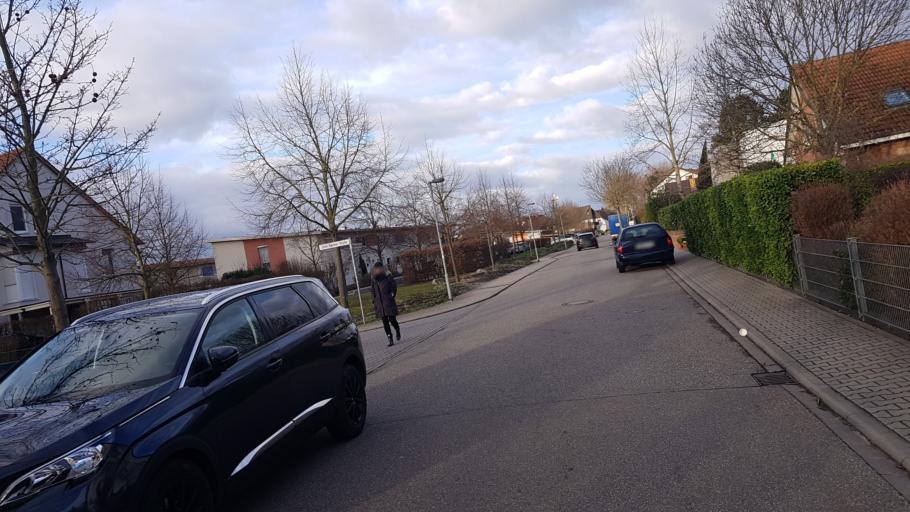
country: DE
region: Baden-Wuerttemberg
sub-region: Karlsruhe Region
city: Walldorf
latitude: 49.3006
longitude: 8.6544
